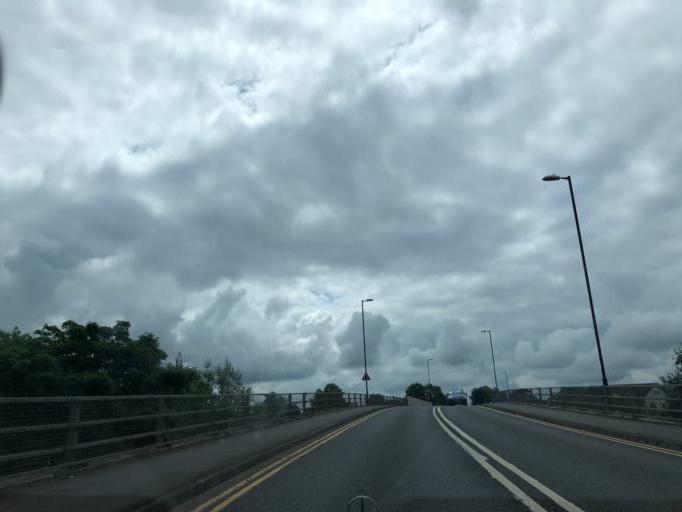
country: GB
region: England
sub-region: Solihull
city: Berkswell
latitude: 52.3964
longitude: -1.5956
